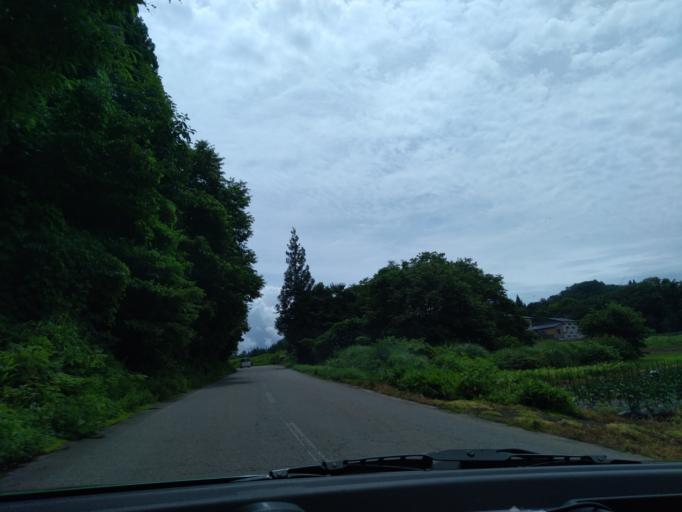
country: JP
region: Akita
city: Kakunodatemachi
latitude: 39.5807
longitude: 140.6252
